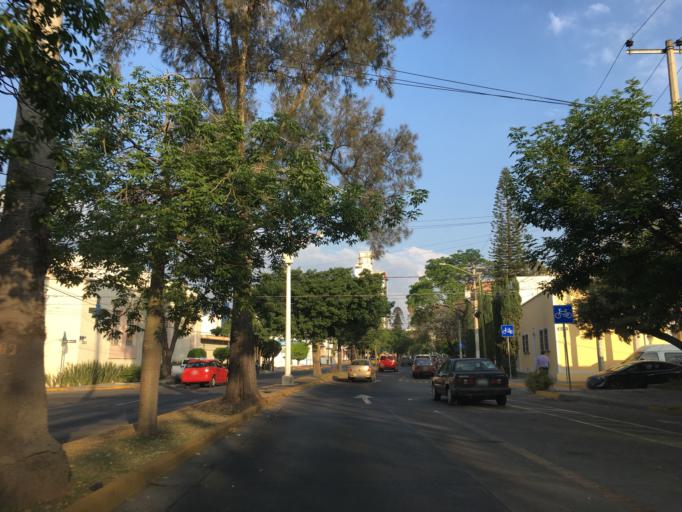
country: MX
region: Jalisco
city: Guadalajara
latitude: 20.6705
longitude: -103.3612
